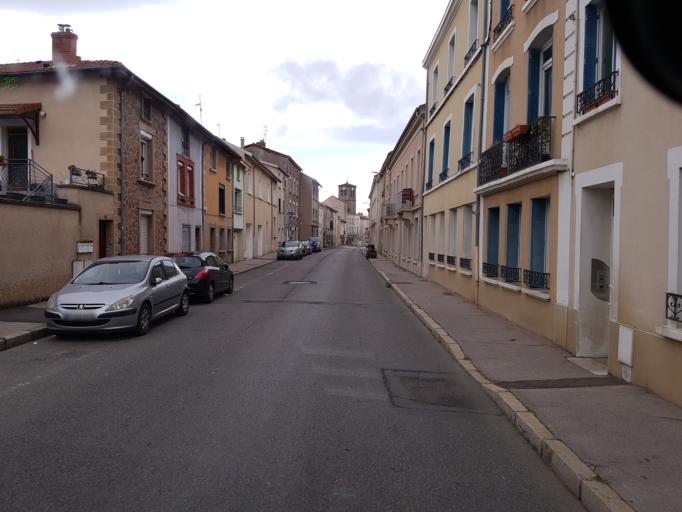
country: FR
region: Rhone-Alpes
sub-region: Departement de la Loire
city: Chazelles-sur-Lyon
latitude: 45.6398
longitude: 4.3932
